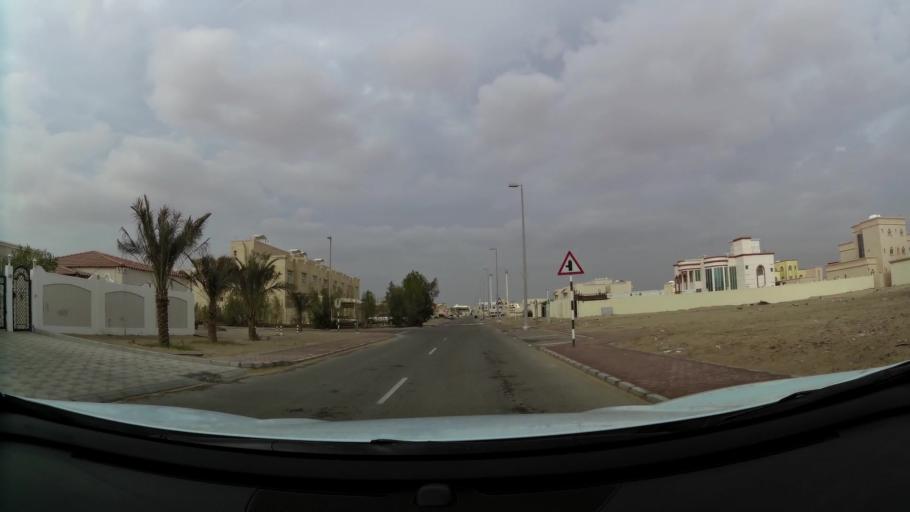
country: AE
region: Abu Dhabi
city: Abu Dhabi
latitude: 24.3401
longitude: 54.6236
